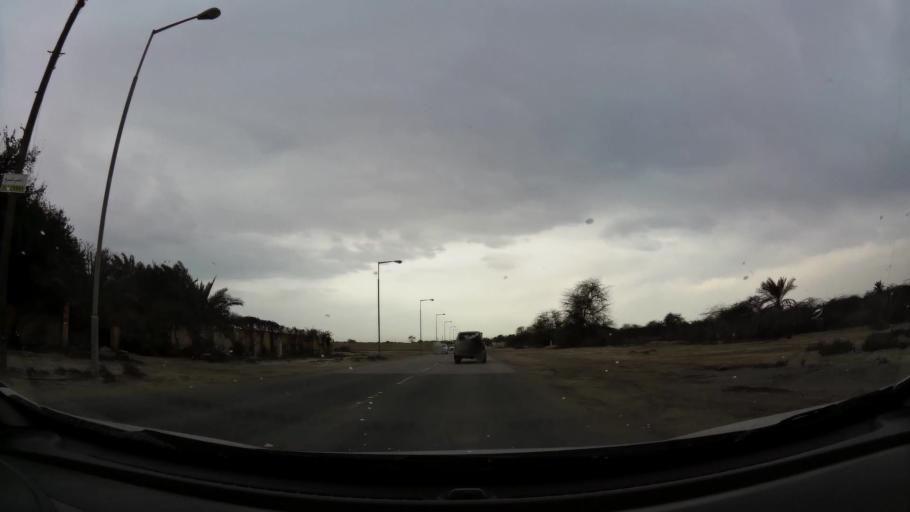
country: BH
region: Central Governorate
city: Madinat Hamad
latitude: 26.1652
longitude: 50.4572
